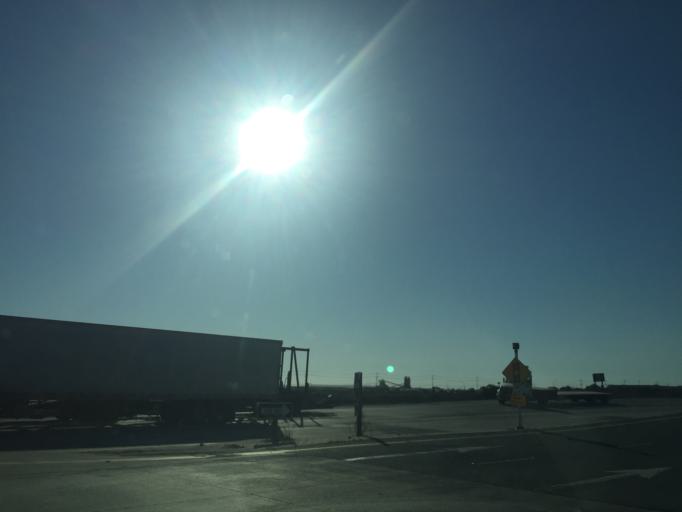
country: MX
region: Baja California
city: Tijuana
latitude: 32.5632
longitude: -116.9626
